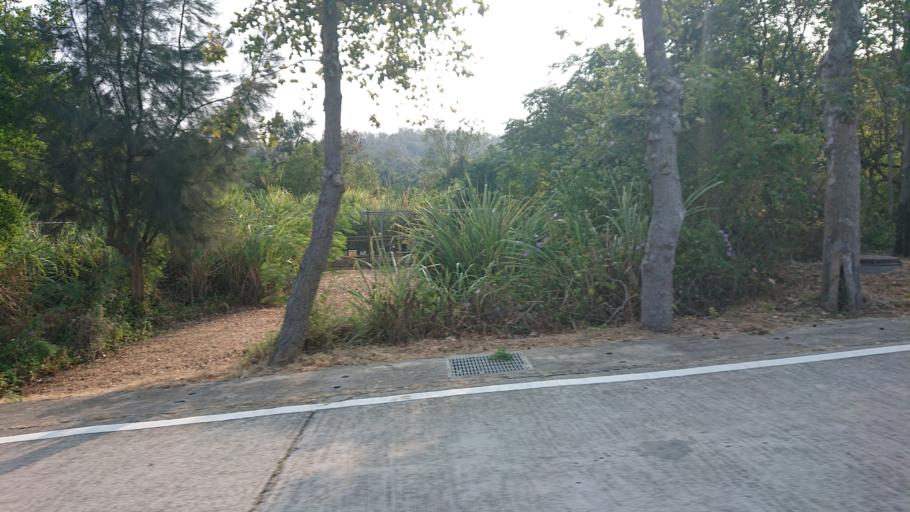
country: CN
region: Fujian
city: Shijing
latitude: 24.5029
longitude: 118.4417
